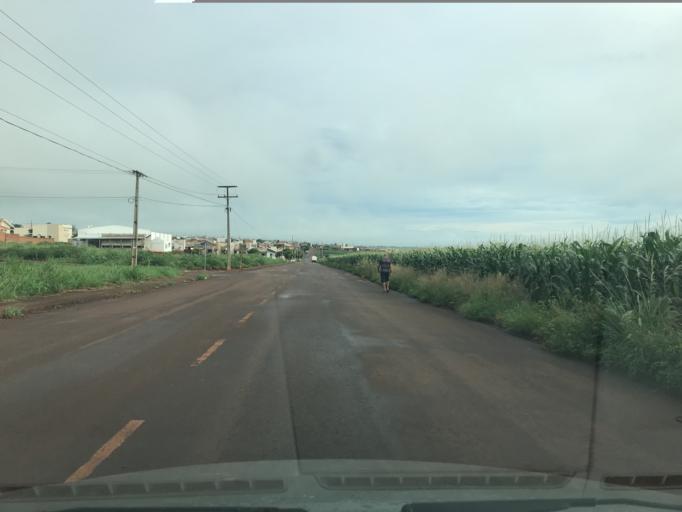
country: BR
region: Parana
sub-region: Palotina
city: Palotina
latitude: -24.3015
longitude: -53.8416
